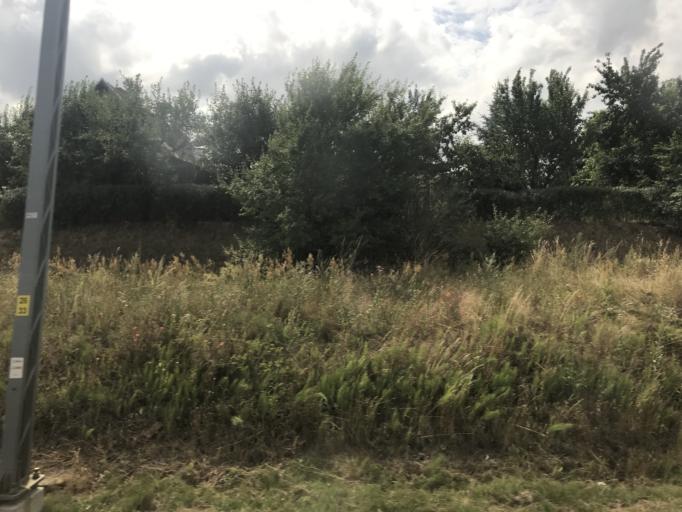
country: PL
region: Greater Poland Voivodeship
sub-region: Powiat poznanski
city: Pobiedziska
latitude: 52.4895
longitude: 17.3513
